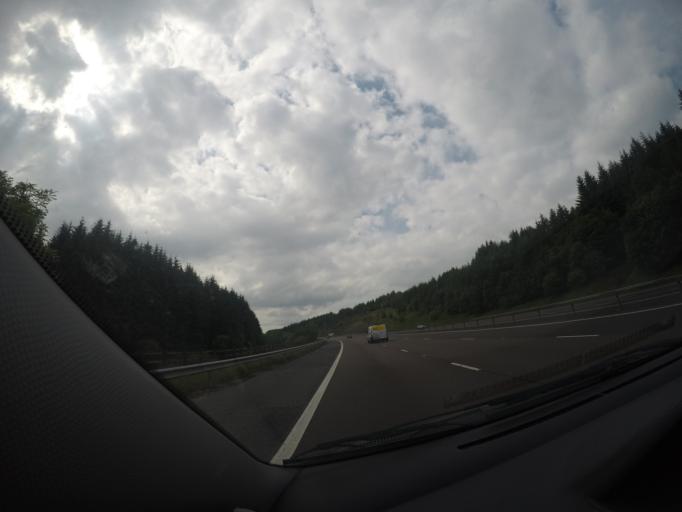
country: GB
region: Scotland
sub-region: Dumfries and Galloway
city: Moffat
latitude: 55.4073
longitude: -3.5601
